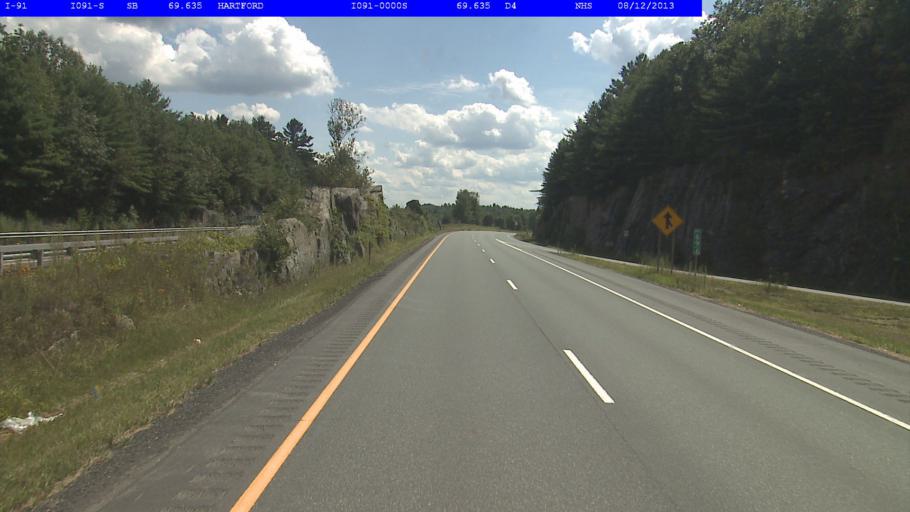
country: US
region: Vermont
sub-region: Windsor County
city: White River Junction
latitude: 43.6374
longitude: -72.3387
